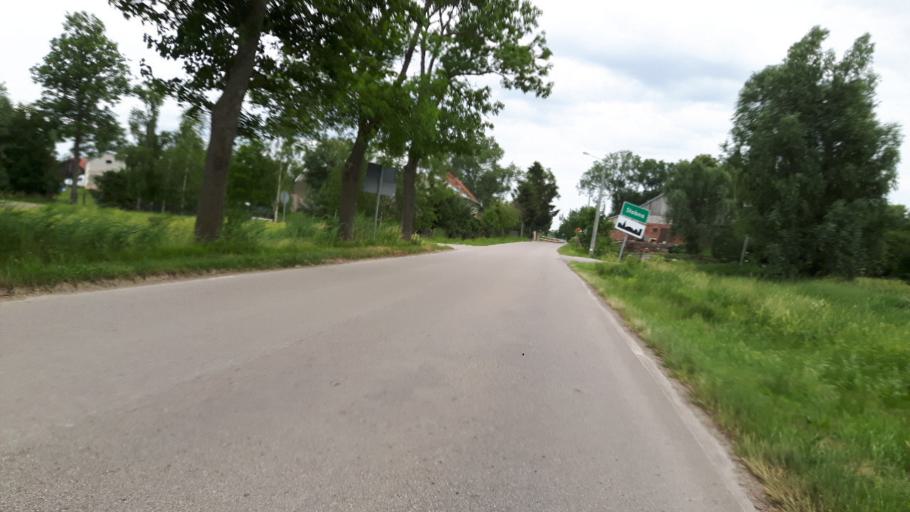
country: PL
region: Warmian-Masurian Voivodeship
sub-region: Powiat elblaski
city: Gronowo Elblaskie
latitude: 54.2027
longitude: 19.2795
